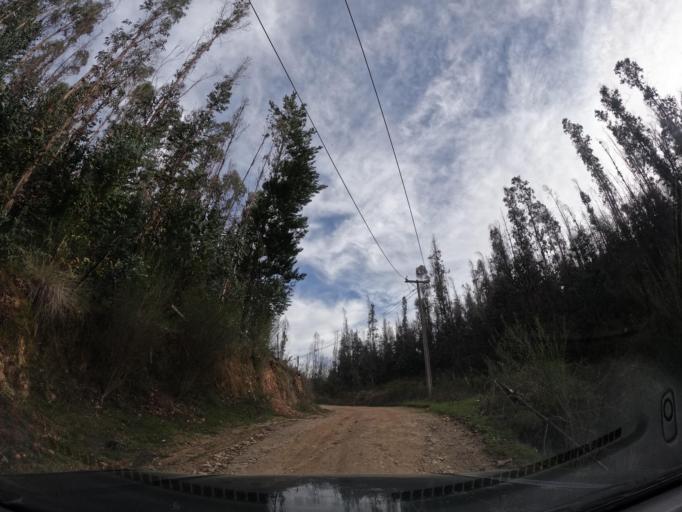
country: CL
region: Biobio
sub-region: Provincia de Concepcion
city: Chiguayante
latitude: -37.0194
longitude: -72.9141
